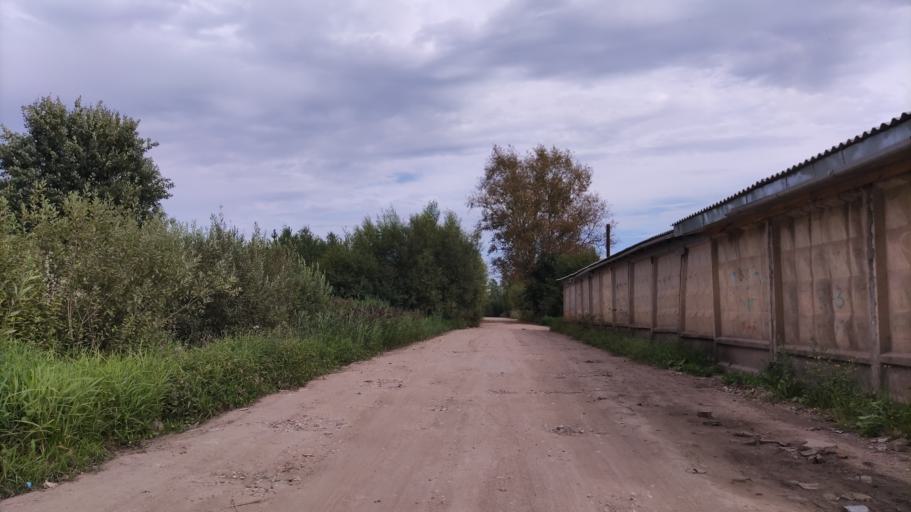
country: RU
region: Tverskaya
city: Rzhev
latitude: 56.2383
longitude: 34.3197
